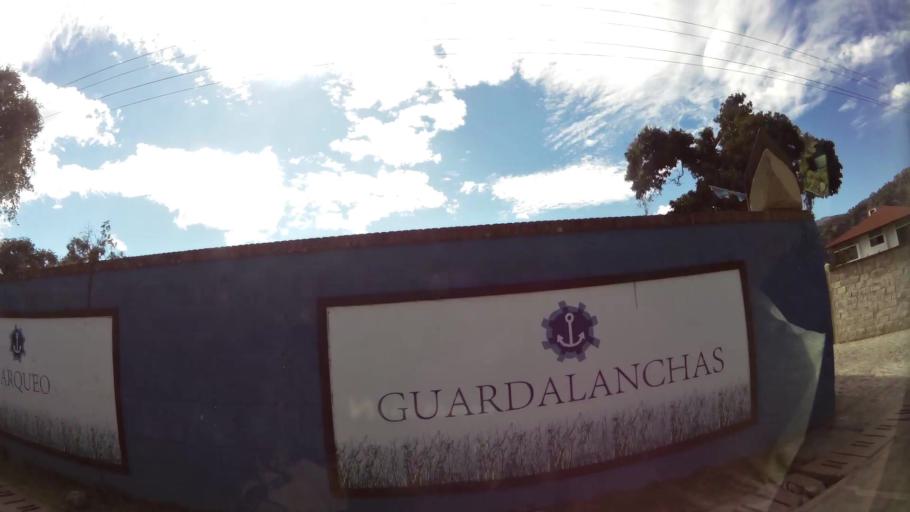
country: GT
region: Solola
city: Panajachel
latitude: 14.7413
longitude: -91.1622
